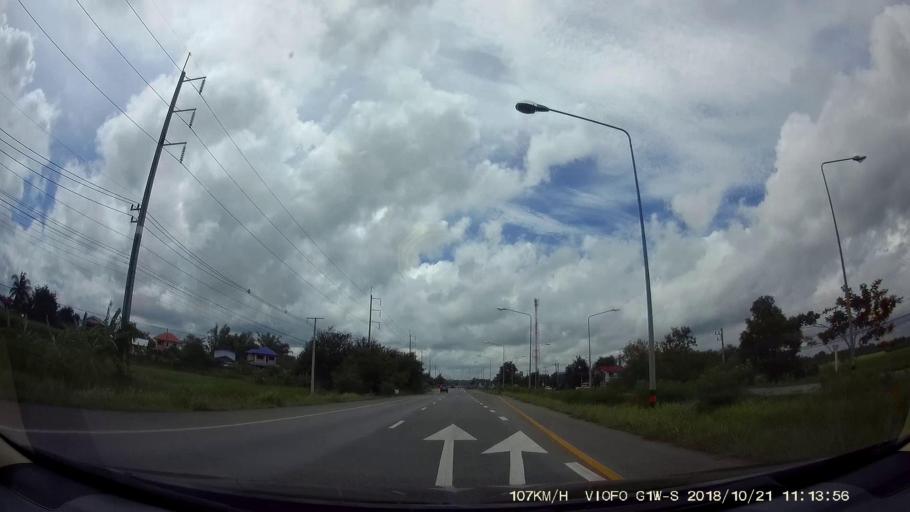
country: TH
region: Chaiyaphum
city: Chaiyaphum
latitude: 15.9102
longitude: 102.1275
